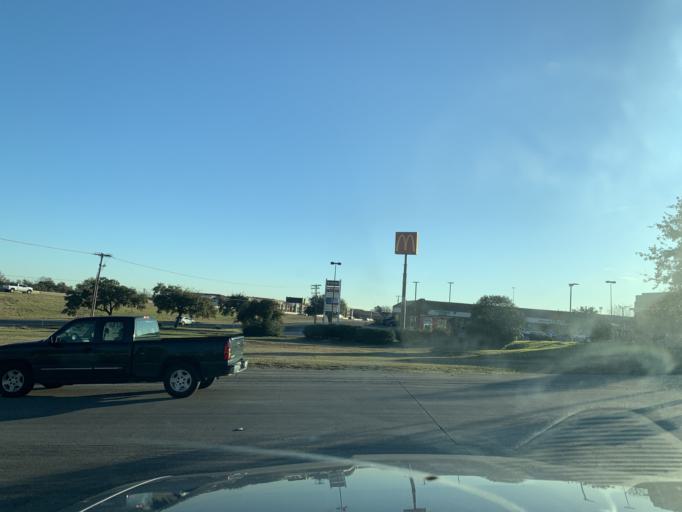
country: US
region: Texas
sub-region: Tarrant County
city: Bedford
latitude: 32.8519
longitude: -97.1124
